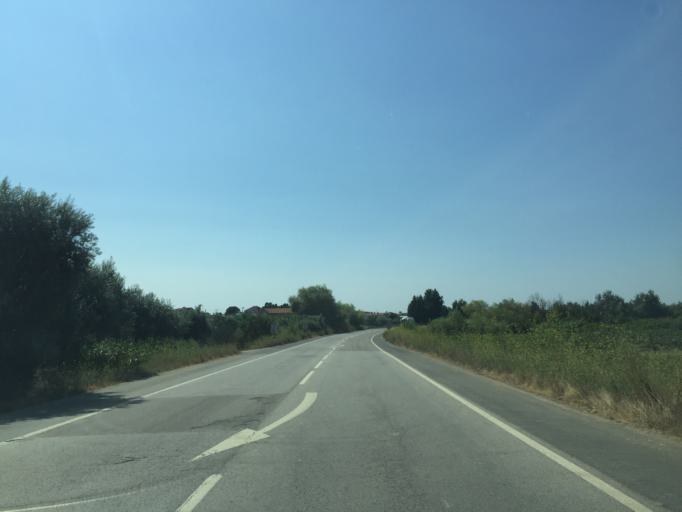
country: PT
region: Aveiro
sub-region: Mealhada
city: Mealhada
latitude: 40.3694
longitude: -8.4641
